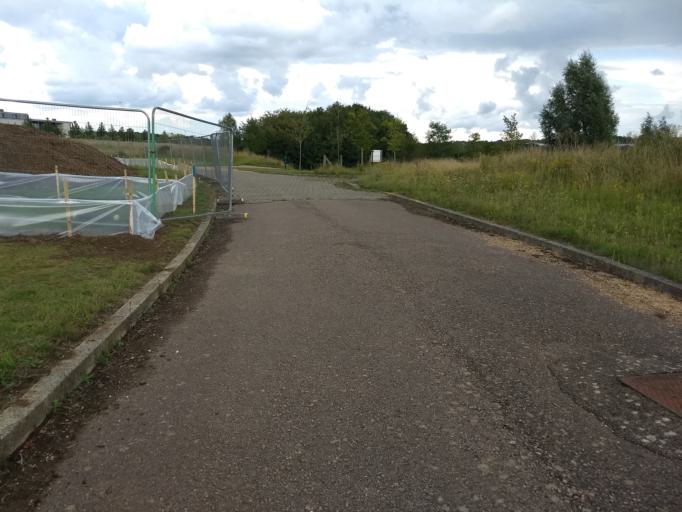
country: GB
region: England
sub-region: Milton Keynes
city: Shenley Church End
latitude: 51.9912
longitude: -0.8023
